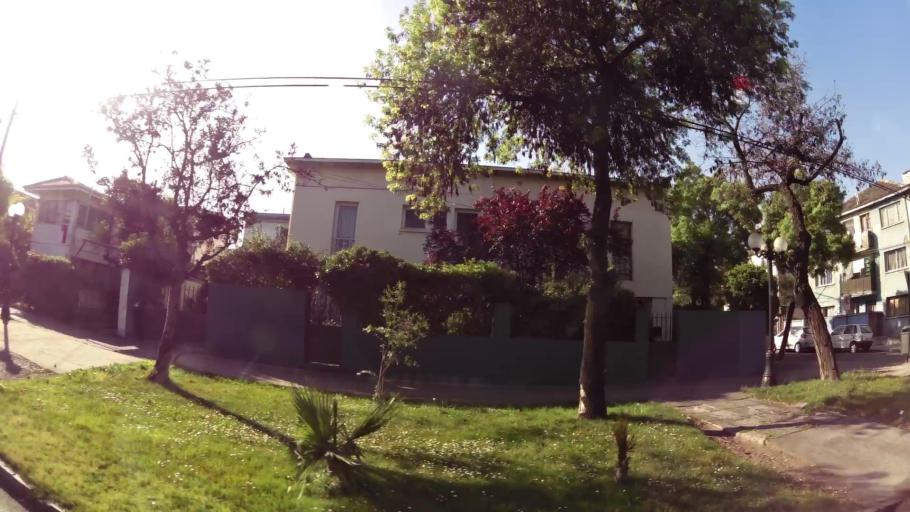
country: CL
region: Santiago Metropolitan
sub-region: Provincia de Santiago
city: Villa Presidente Frei, Nunoa, Santiago, Chile
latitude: -33.4455
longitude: -70.6074
